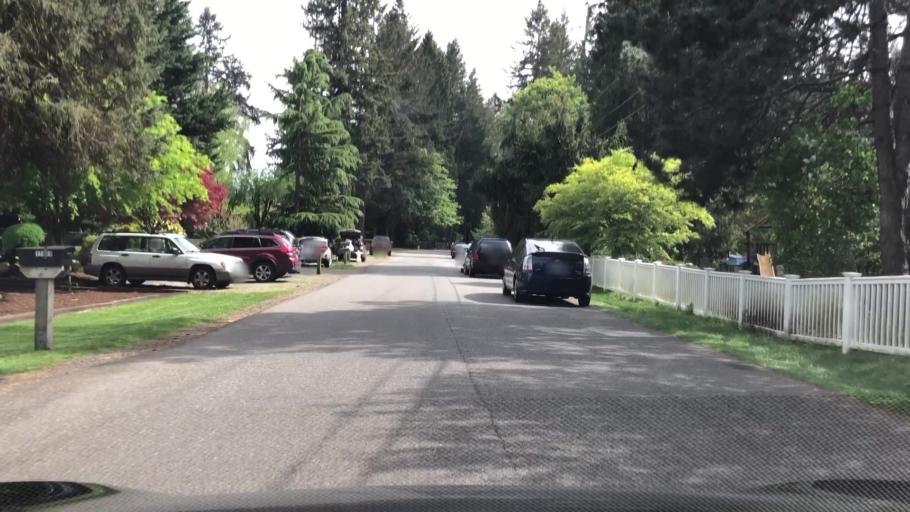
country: US
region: Washington
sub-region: King County
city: Cottage Lake
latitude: 47.7555
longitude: -122.0928
